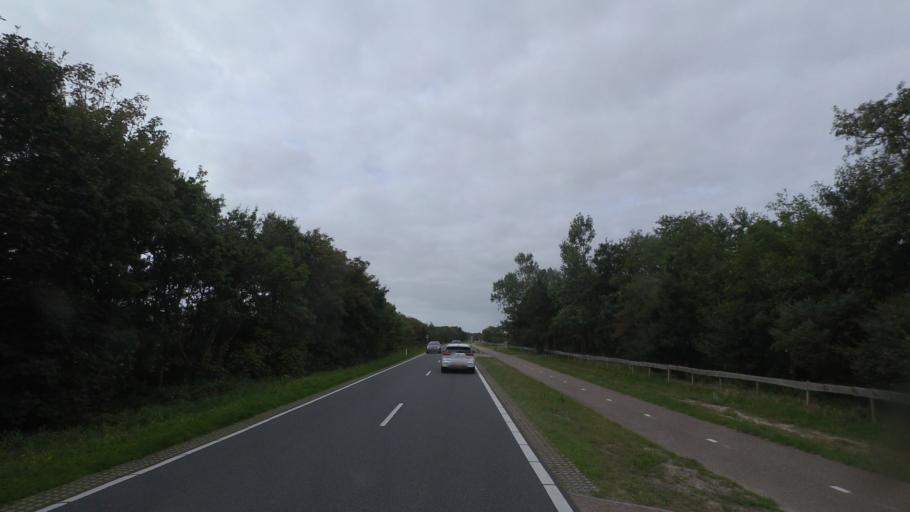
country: NL
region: Friesland
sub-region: Gemeente Ameland
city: Nes
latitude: 53.4455
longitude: 5.7274
